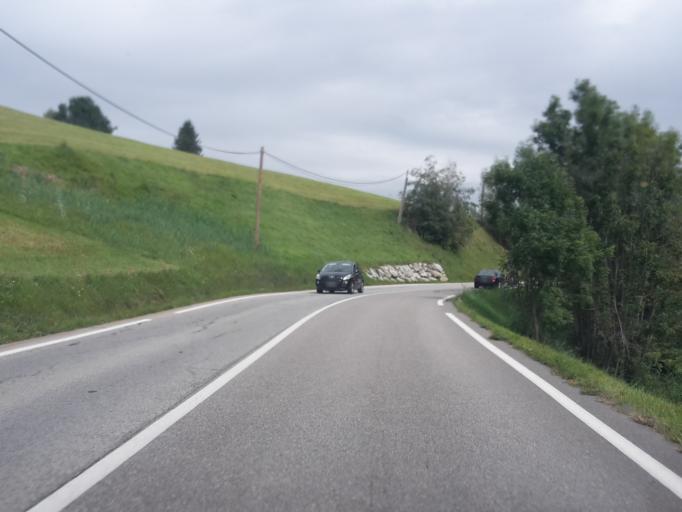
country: FR
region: Rhone-Alpes
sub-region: Departement de la Haute-Savoie
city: Praz-sur-Arly
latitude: 45.8271
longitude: 6.5427
